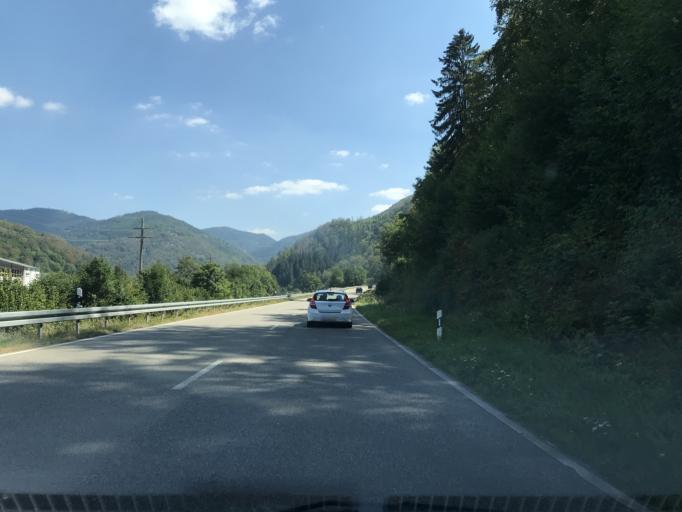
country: DE
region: Baden-Wuerttemberg
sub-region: Freiburg Region
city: Utzenfeld
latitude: 47.7984
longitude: 7.9103
